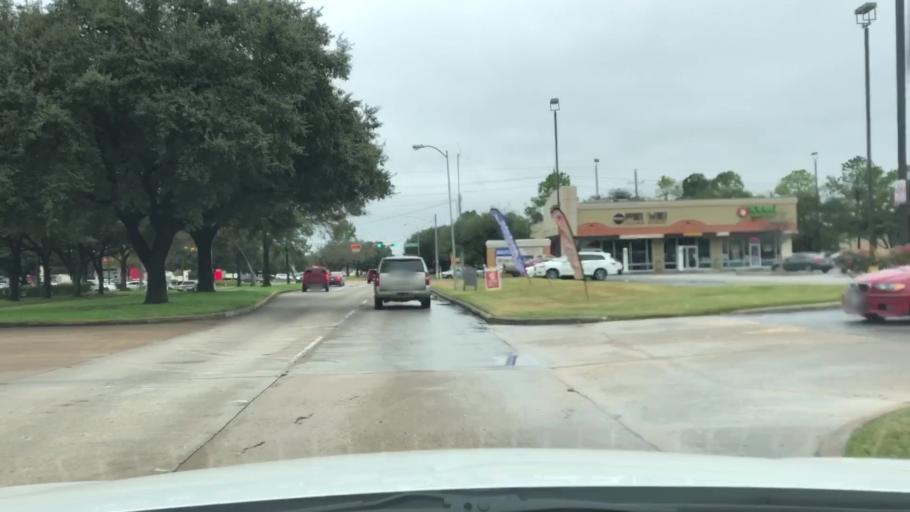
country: US
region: Texas
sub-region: Fort Bend County
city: Cinco Ranch
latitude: 29.7597
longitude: -95.7517
